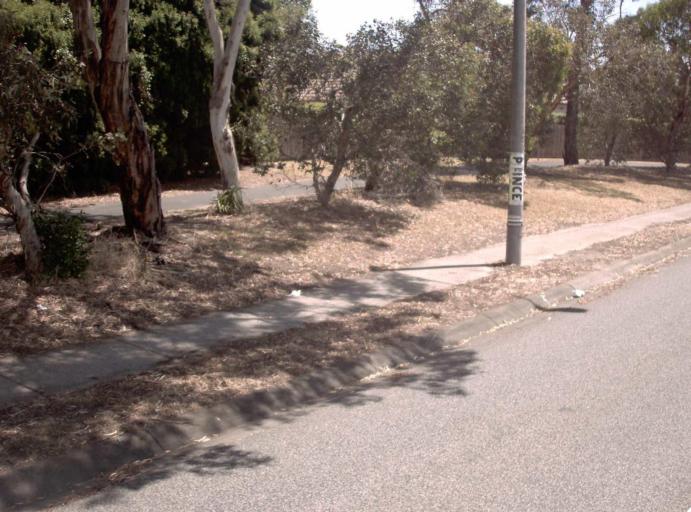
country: AU
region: Victoria
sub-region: Bayside
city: North Brighton
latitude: -37.9005
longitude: 145.0063
